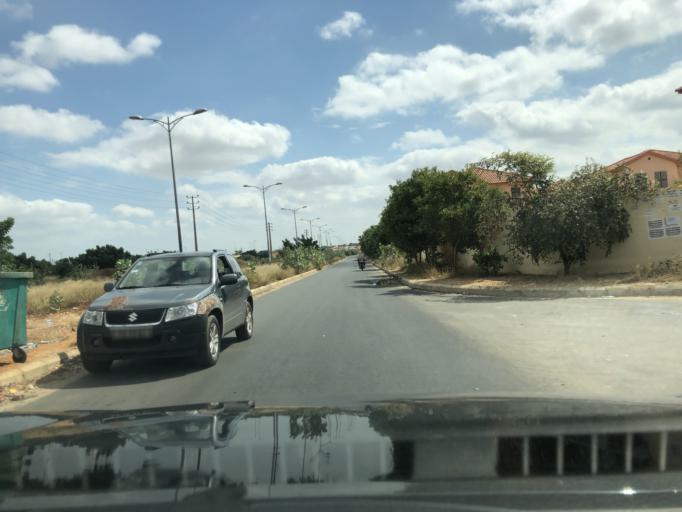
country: AO
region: Luanda
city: Luanda
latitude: -8.9479
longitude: 13.2426
